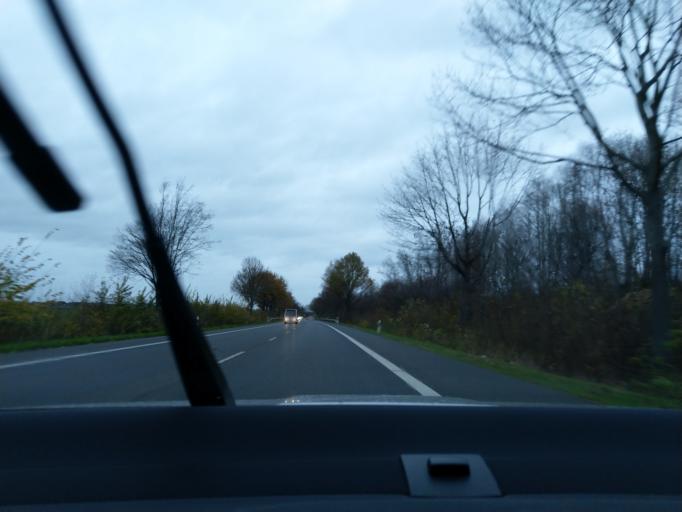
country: DE
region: North Rhine-Westphalia
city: Erkelenz
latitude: 51.0725
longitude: 6.3005
